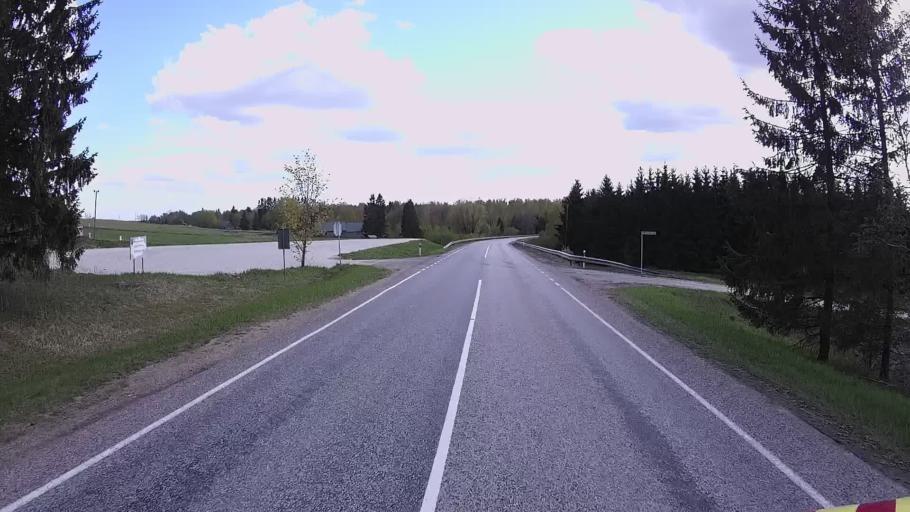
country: EE
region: Jogevamaa
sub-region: Jogeva linn
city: Jogeva
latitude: 58.7780
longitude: 26.4728
